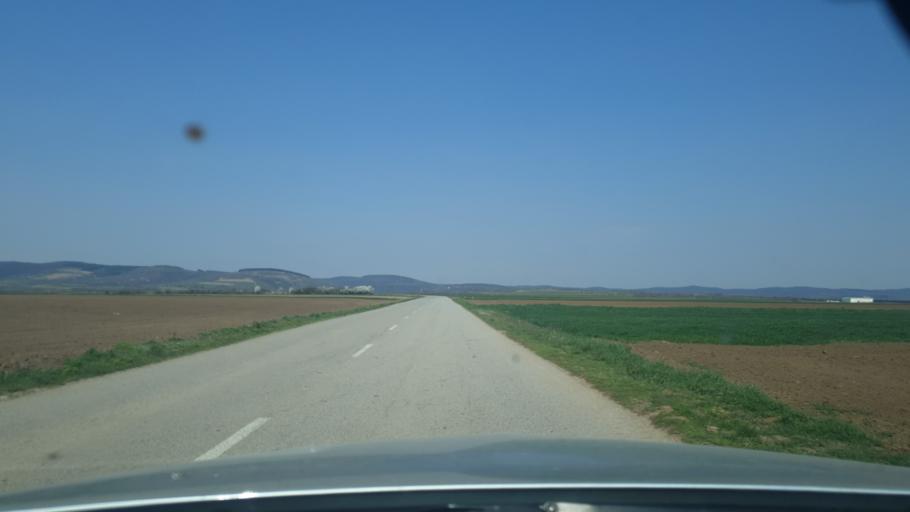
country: RS
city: Vrdnik
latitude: 45.0800
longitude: 19.7697
